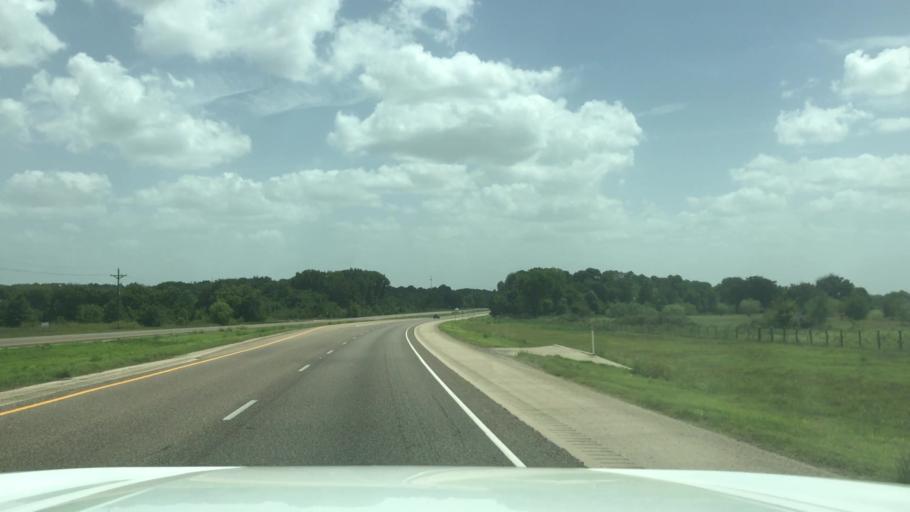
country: US
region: Texas
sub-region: Robertson County
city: Calvert
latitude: 31.1223
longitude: -96.7126
